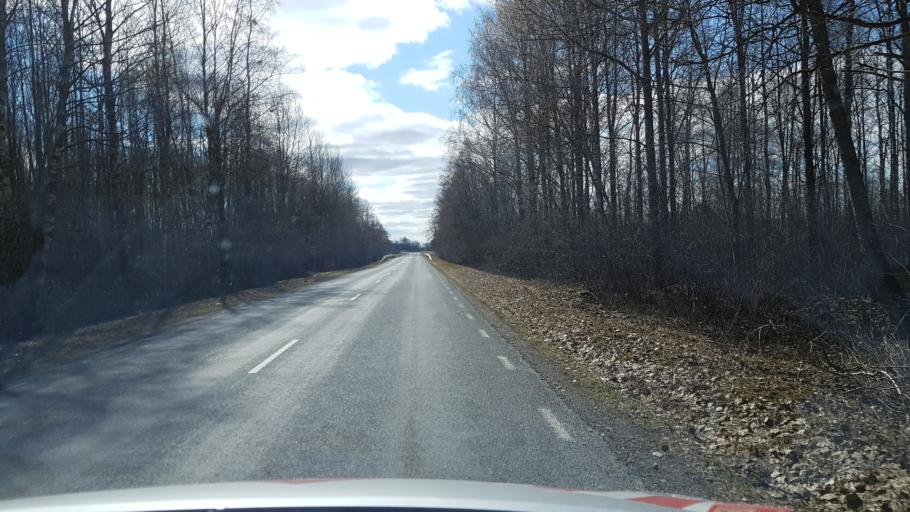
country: EE
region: Laeaene-Virumaa
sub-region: Tapa vald
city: Tapa
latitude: 59.2620
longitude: 25.8462
